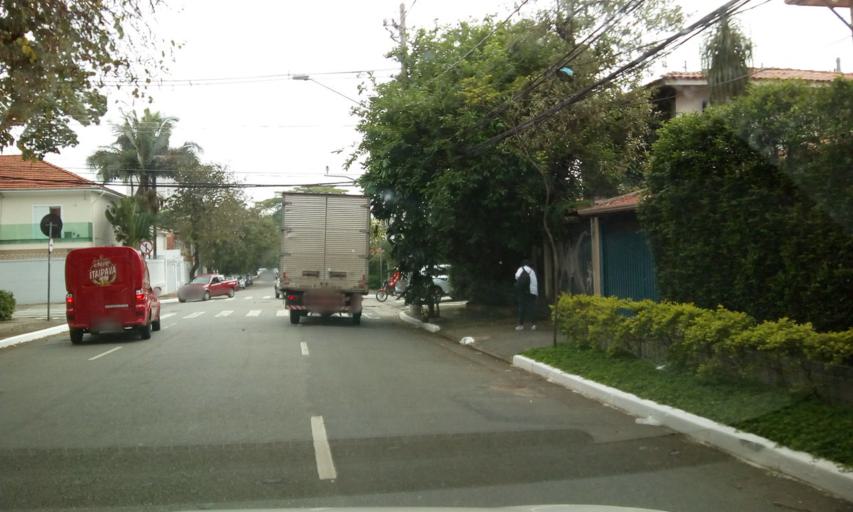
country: BR
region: Sao Paulo
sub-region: Sao Paulo
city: Sao Paulo
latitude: -23.6101
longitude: -46.6703
